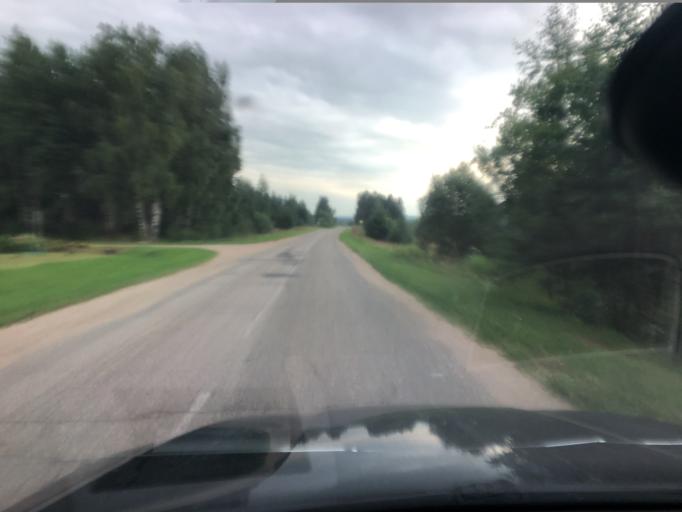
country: RU
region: Jaroslavl
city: Pereslavl'-Zalesskiy
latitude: 57.0112
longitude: 38.9713
